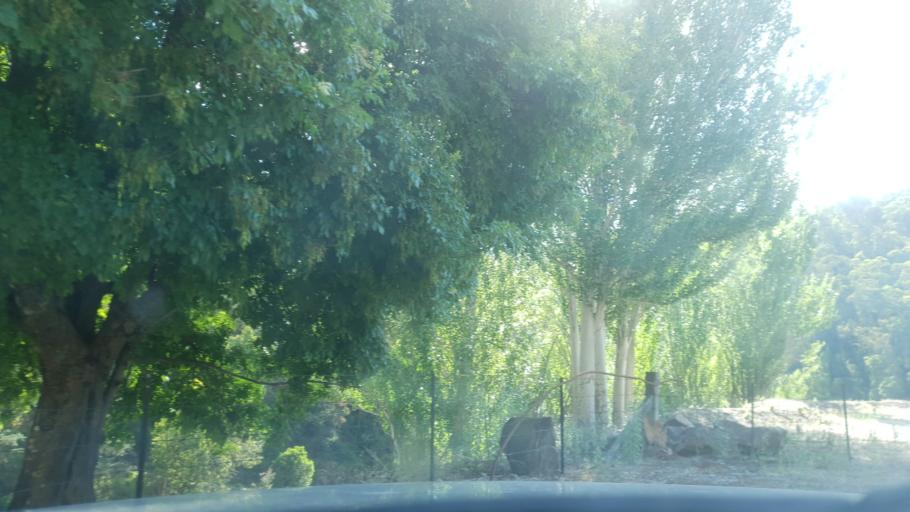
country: AU
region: Victoria
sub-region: Alpine
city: Mount Beauty
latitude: -36.7604
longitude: 147.1862
